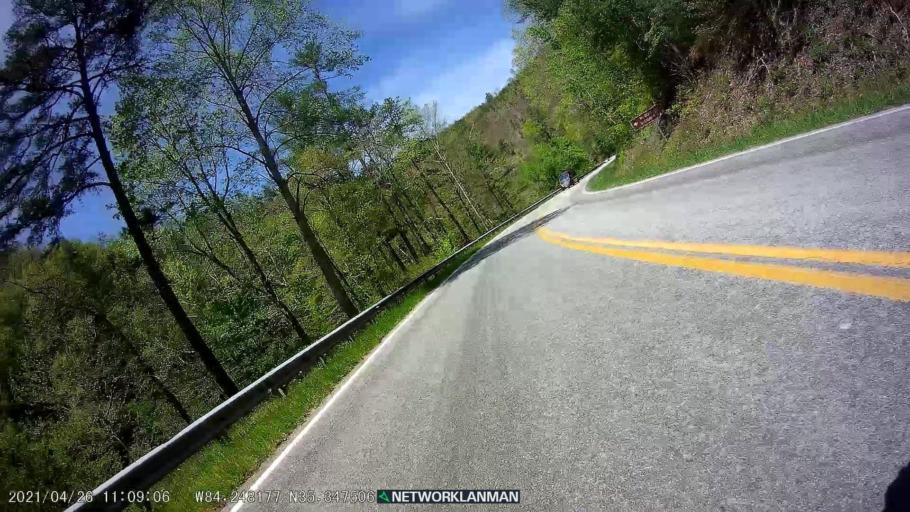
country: US
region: Tennessee
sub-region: Monroe County
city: Madisonville
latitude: 35.3473
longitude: -84.2481
